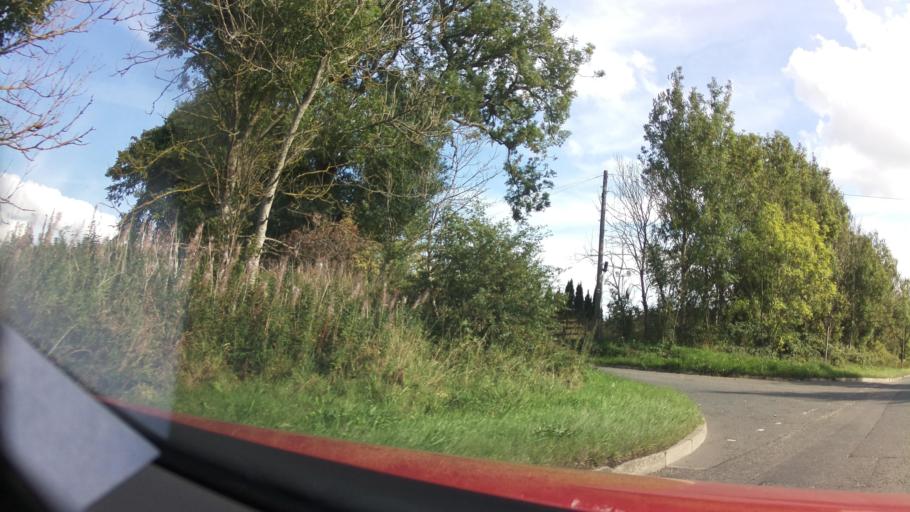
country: GB
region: Scotland
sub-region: Stirling
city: Cowie
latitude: 56.0530
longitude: -3.8608
